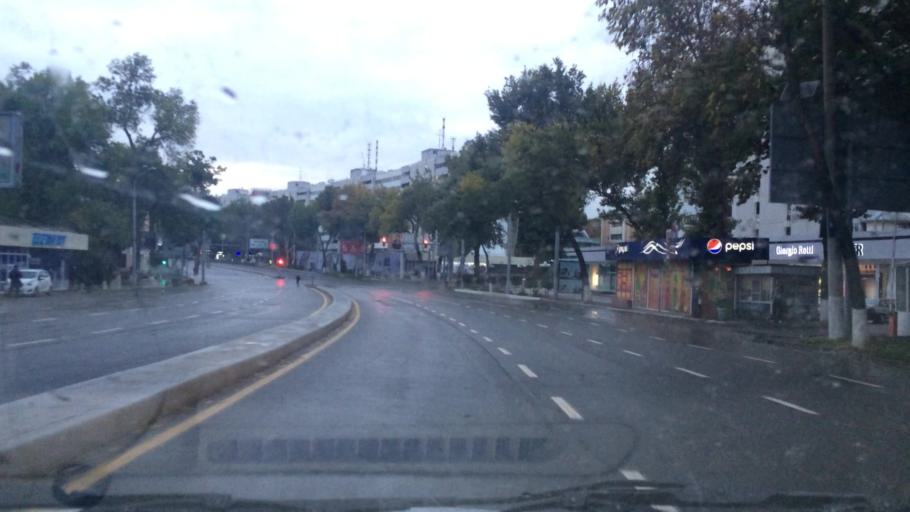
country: UZ
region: Toshkent Shahri
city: Tashkent
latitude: 41.3127
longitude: 69.2869
